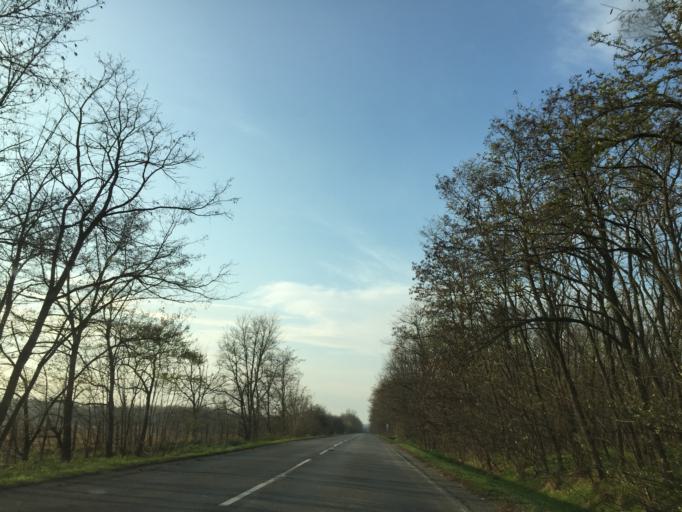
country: SK
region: Nitriansky
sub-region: Okres Komarno
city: Hurbanovo
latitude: 47.9262
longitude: 18.2228
